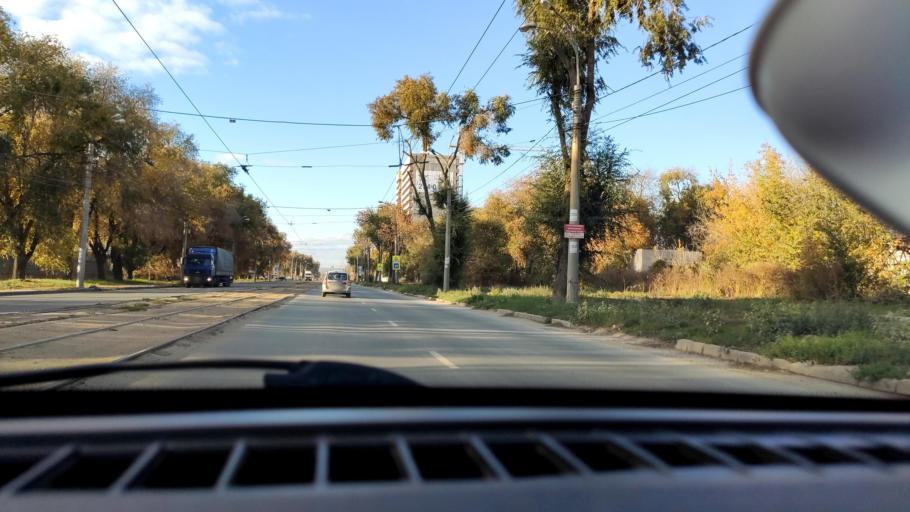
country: RU
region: Samara
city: Smyshlyayevka
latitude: 53.1997
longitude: 50.2861
